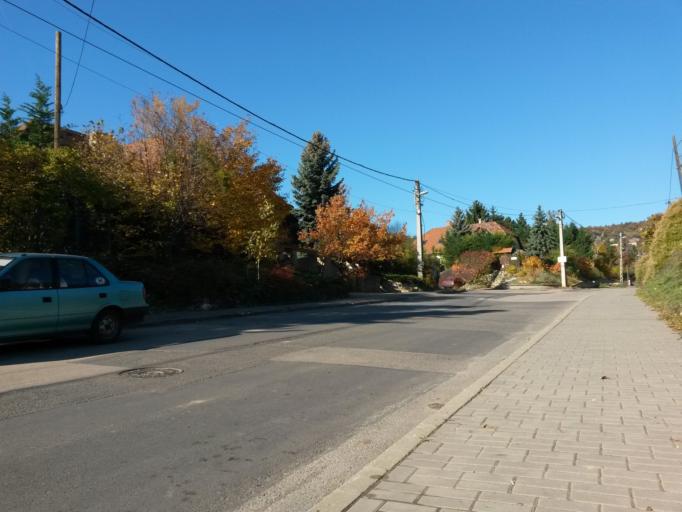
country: HU
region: Pest
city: Budaors
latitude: 47.4770
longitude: 18.9858
